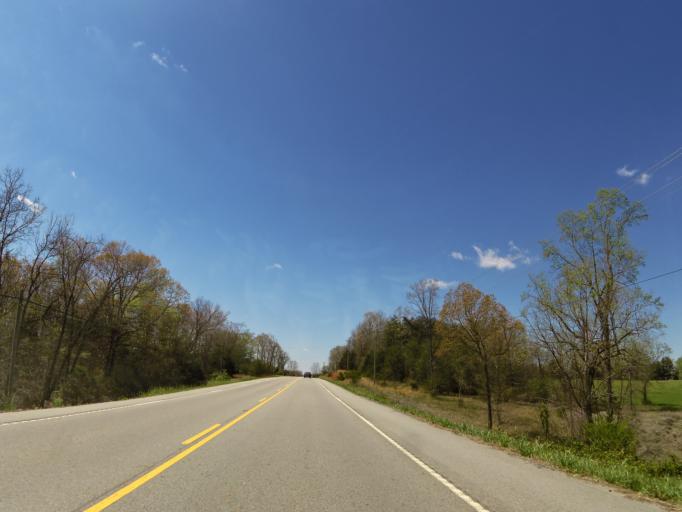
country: US
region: Tennessee
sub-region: White County
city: Sparta
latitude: 35.9613
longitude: -85.6195
